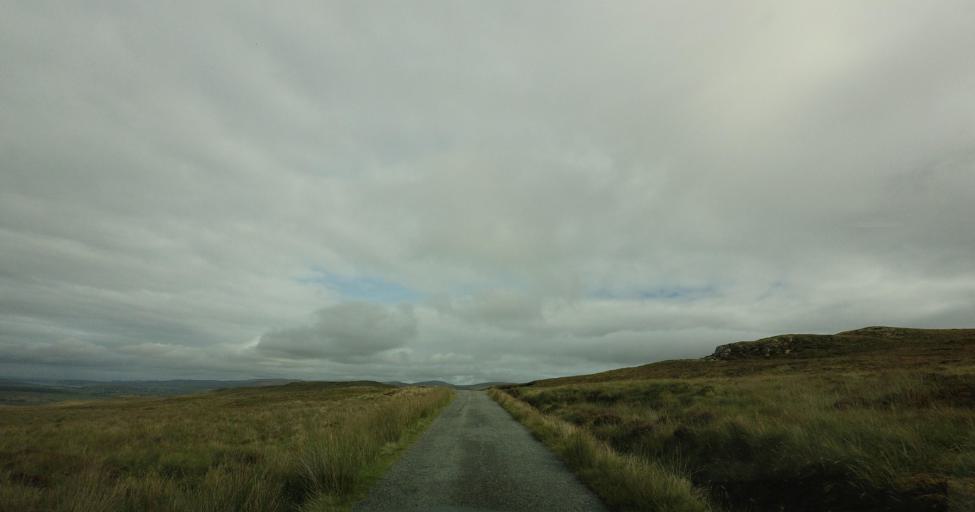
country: GB
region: Scotland
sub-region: Highland
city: Isle of Skye
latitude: 57.4051
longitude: -6.2668
